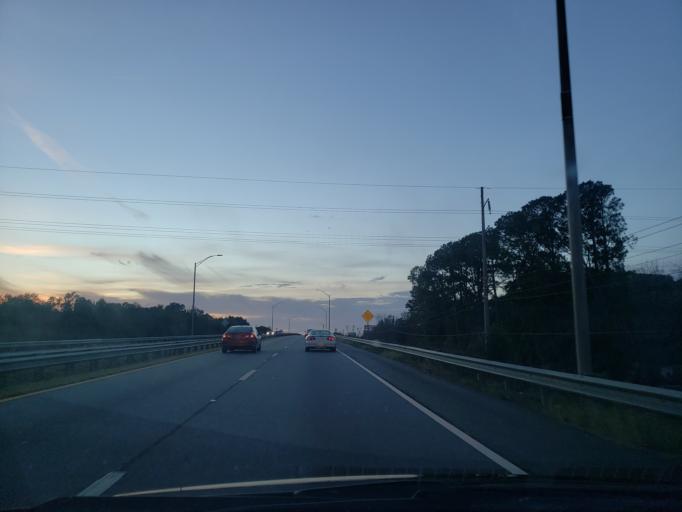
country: US
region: Georgia
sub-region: Dougherty County
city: Albany
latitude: 31.5725
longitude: -84.1191
